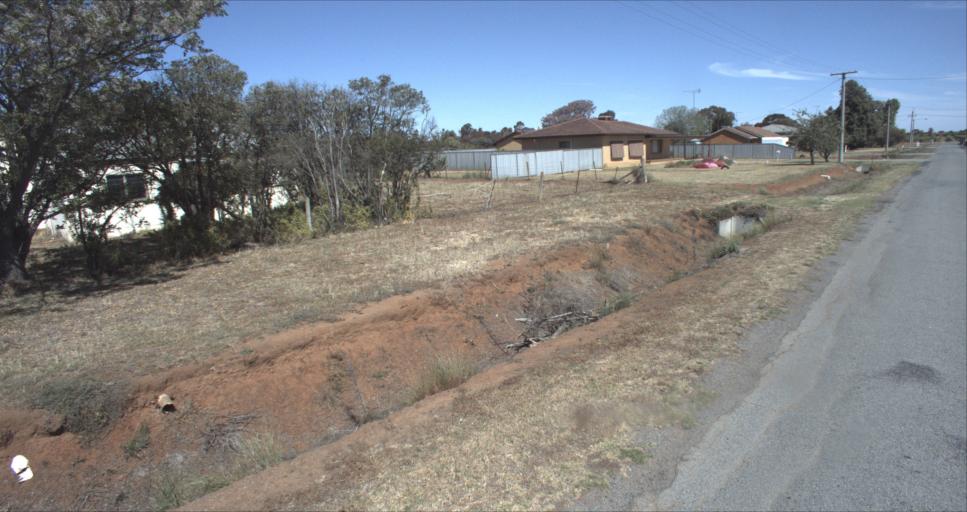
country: AU
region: New South Wales
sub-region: Leeton
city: Leeton
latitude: -34.5530
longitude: 146.3807
